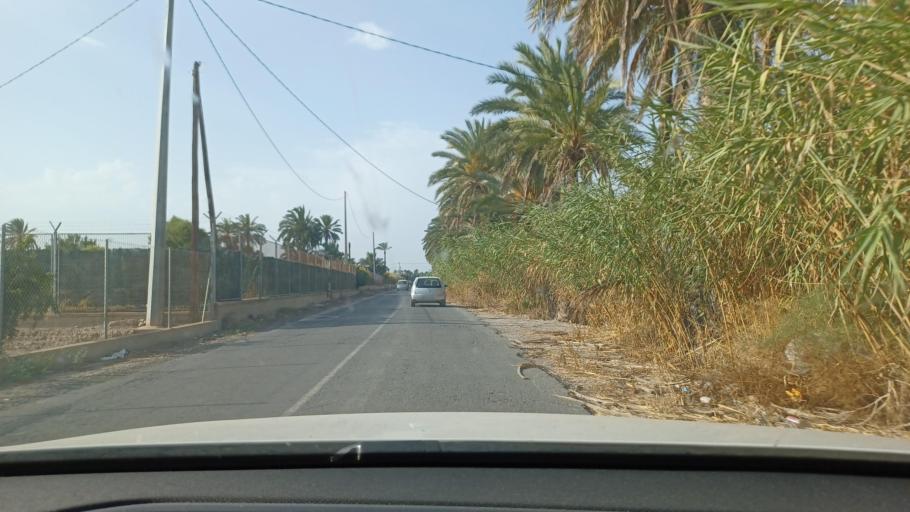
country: ES
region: Valencia
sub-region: Provincia de Alicante
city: Elche
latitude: 38.2241
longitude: -0.6950
